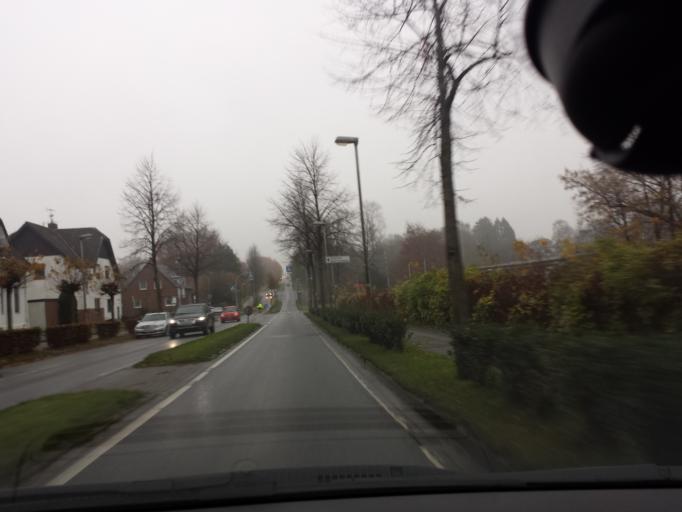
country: DE
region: North Rhine-Westphalia
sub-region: Regierungsbezirk Koln
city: Herzogenrath
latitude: 50.8931
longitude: 6.1271
